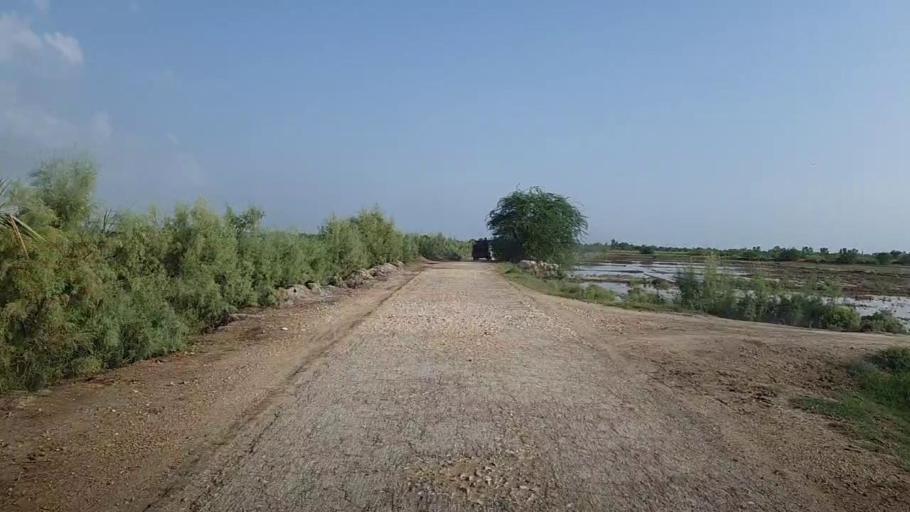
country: PK
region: Sindh
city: Pad Idan
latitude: 26.8244
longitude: 68.2380
